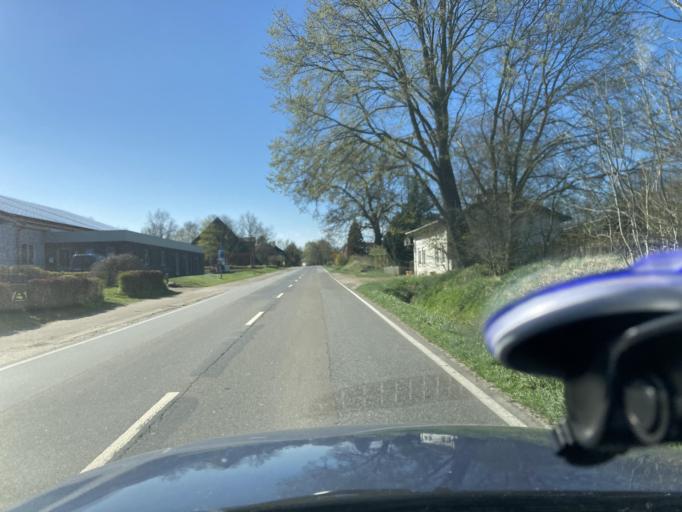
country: DE
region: Schleswig-Holstein
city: Odderade
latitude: 54.1425
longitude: 9.1913
